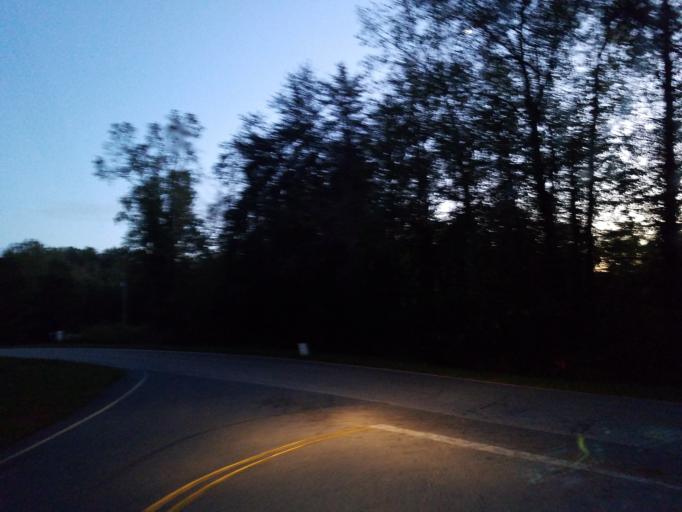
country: US
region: Georgia
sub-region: Dawson County
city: Dawsonville
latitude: 34.5194
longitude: -84.1842
